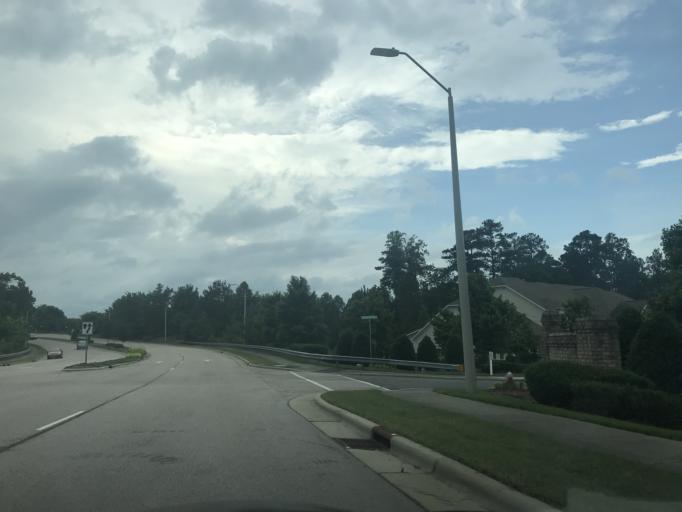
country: US
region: North Carolina
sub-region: Wake County
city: Morrisville
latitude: 35.8143
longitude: -78.8504
